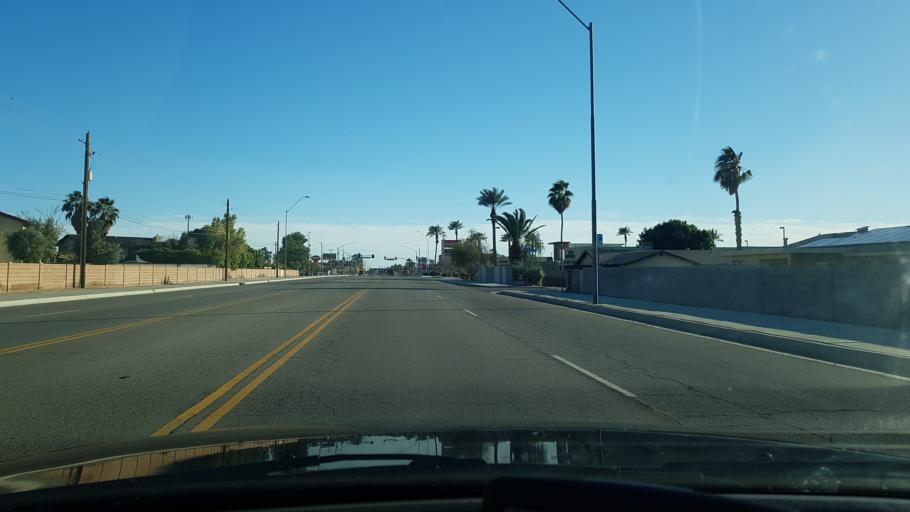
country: US
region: Arizona
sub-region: Yuma County
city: Yuma
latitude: 32.6793
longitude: -114.5988
